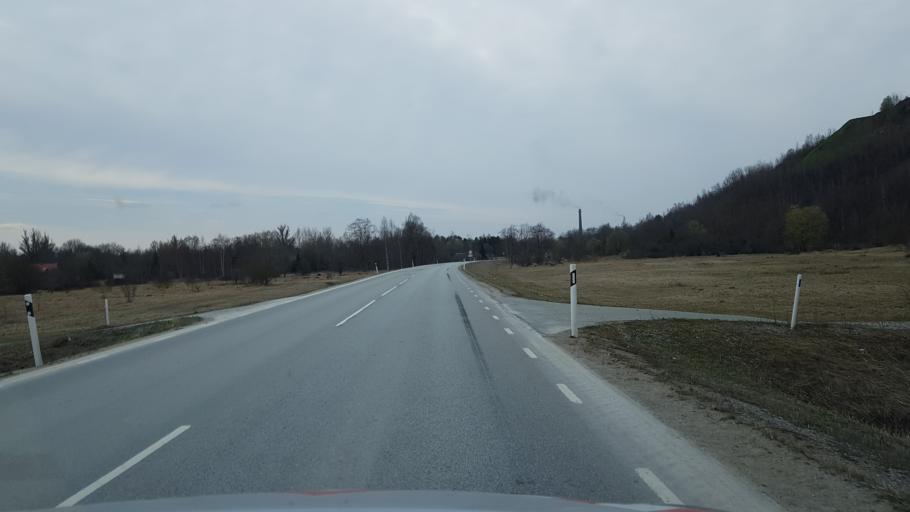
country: EE
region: Ida-Virumaa
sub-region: Kivioli linn
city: Kivioli
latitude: 59.3625
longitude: 26.9613
